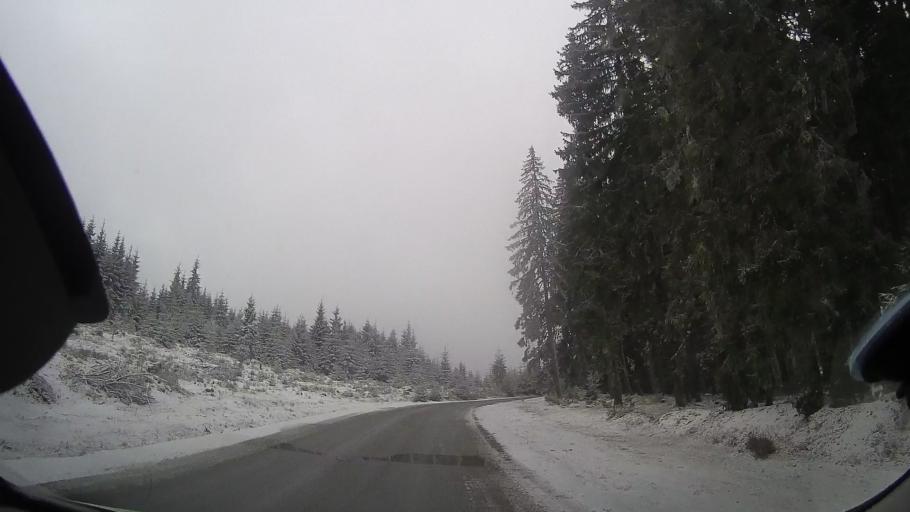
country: RO
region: Cluj
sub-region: Comuna Belis
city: Belis
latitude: 46.6405
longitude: 23.0572
